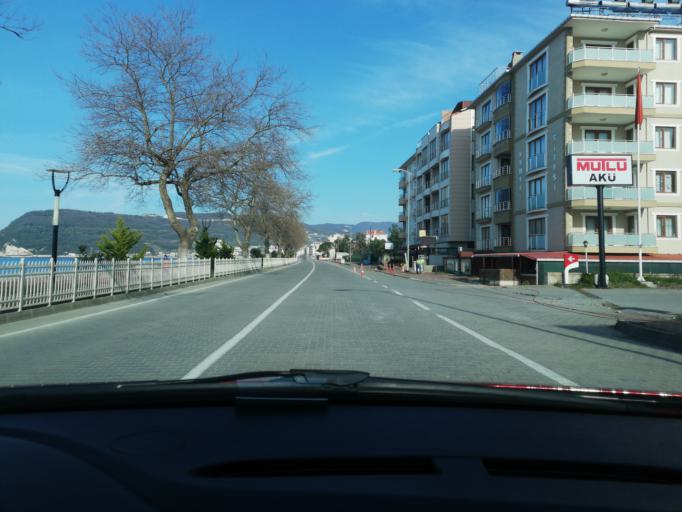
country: TR
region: Kastamonu
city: Cide
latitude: 41.8889
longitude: 32.9675
